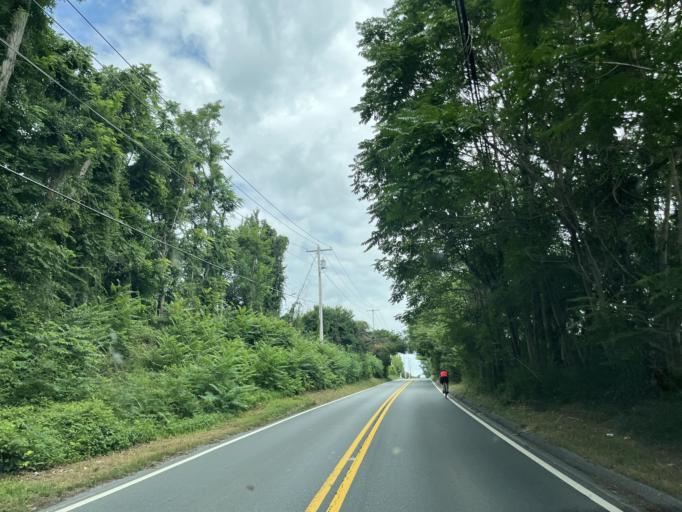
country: US
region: Maryland
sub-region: Montgomery County
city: Damascus
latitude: 39.2366
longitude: -77.1812
